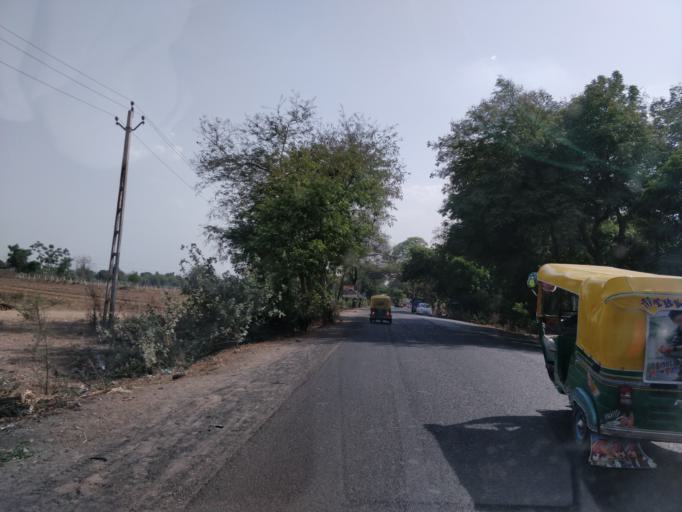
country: IN
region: Gujarat
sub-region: Ahmadabad
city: Naroda
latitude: 23.0953
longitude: 72.6965
